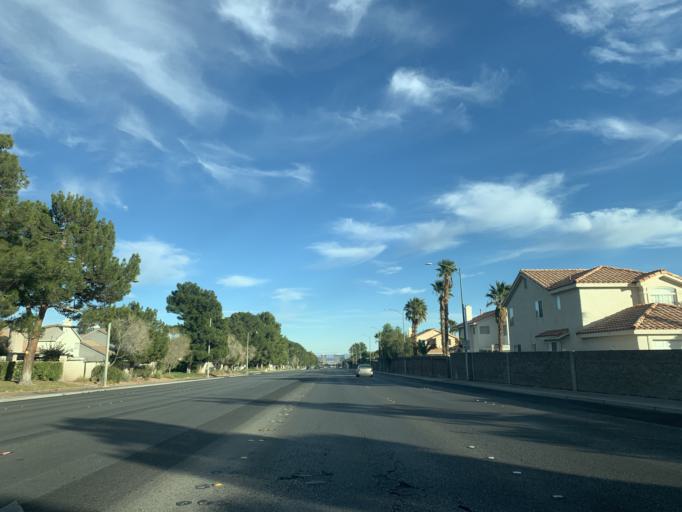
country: US
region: Nevada
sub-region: Clark County
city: Summerlin South
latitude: 36.1296
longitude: -115.2874
